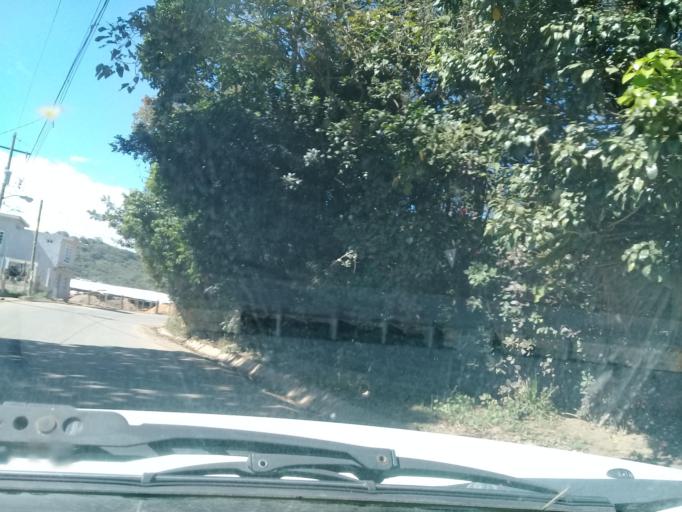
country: MX
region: Veracruz
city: El Castillo
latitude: 19.5506
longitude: -96.8531
